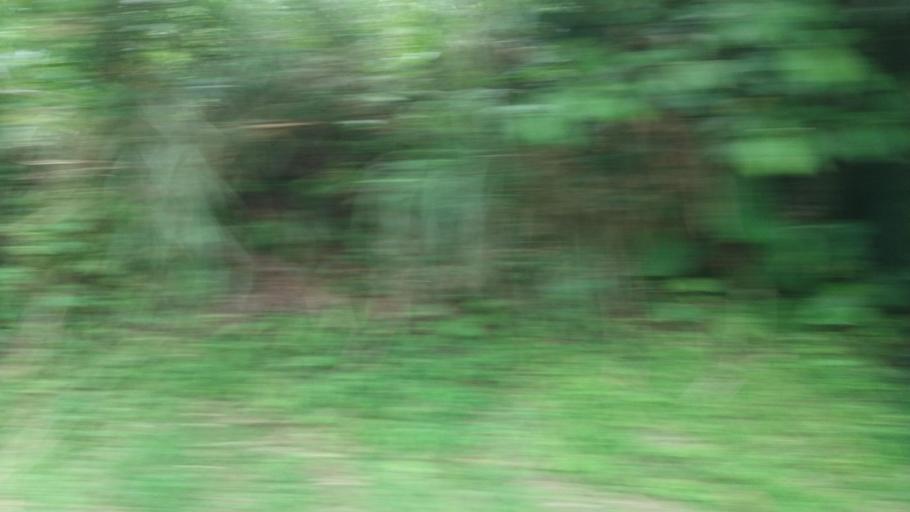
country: TW
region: Taipei
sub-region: Taipei
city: Banqiao
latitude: 24.9178
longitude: 121.4146
